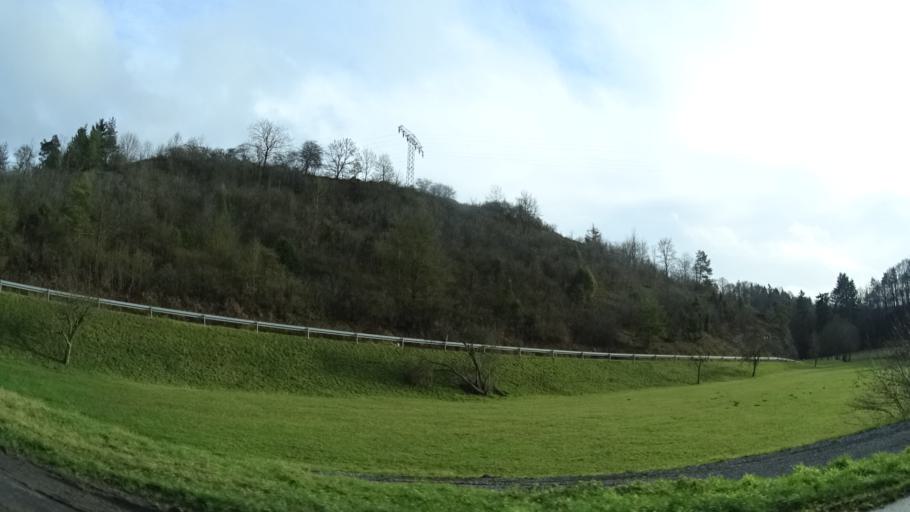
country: DE
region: Thuringia
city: Utendorf
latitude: 50.6037
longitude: 10.4404
